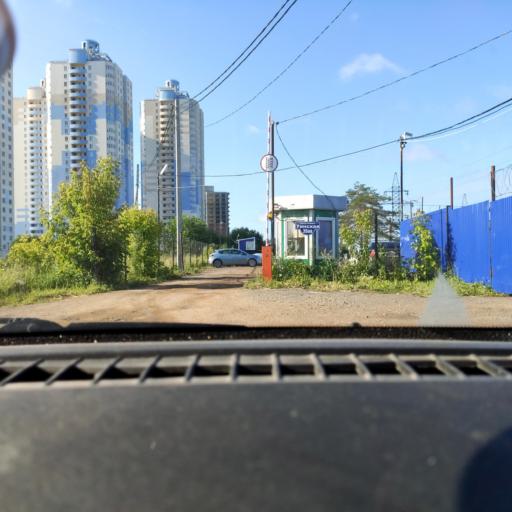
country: RU
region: Perm
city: Perm
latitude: 58.0075
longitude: 56.3199
